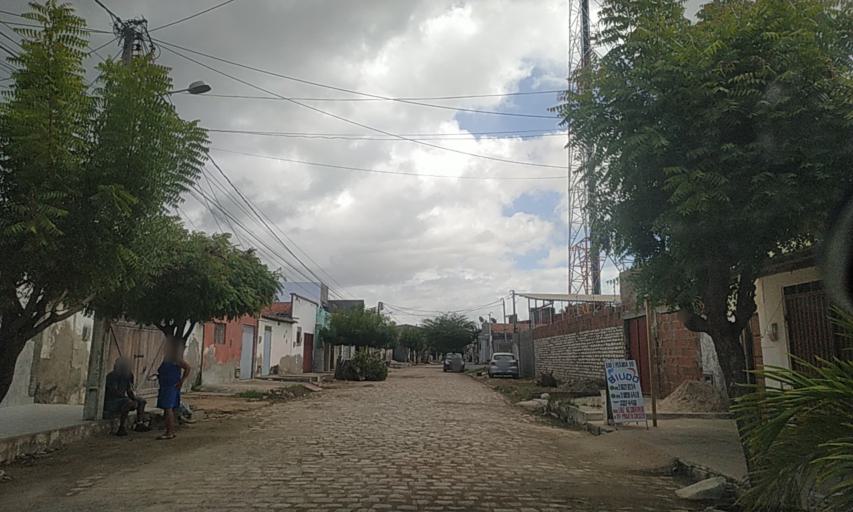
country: BR
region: Rio Grande do Norte
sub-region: Areia Branca
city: Areia Branca
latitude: -4.9524
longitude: -37.1268
